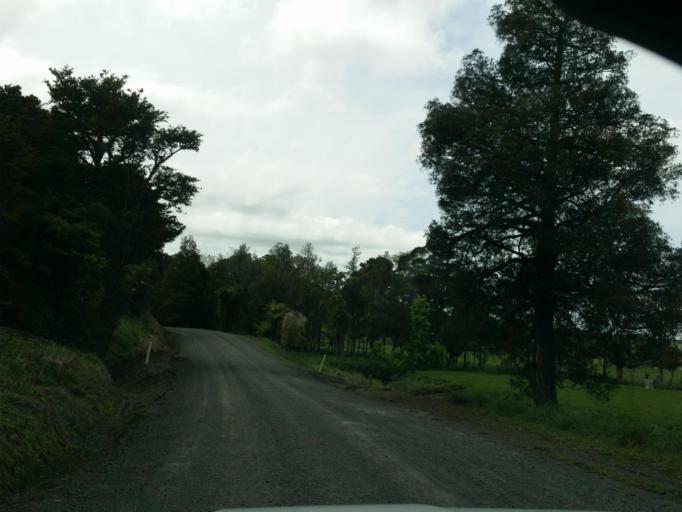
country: NZ
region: Northland
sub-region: Whangarei
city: Maungatapere
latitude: -35.9018
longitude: 174.1503
